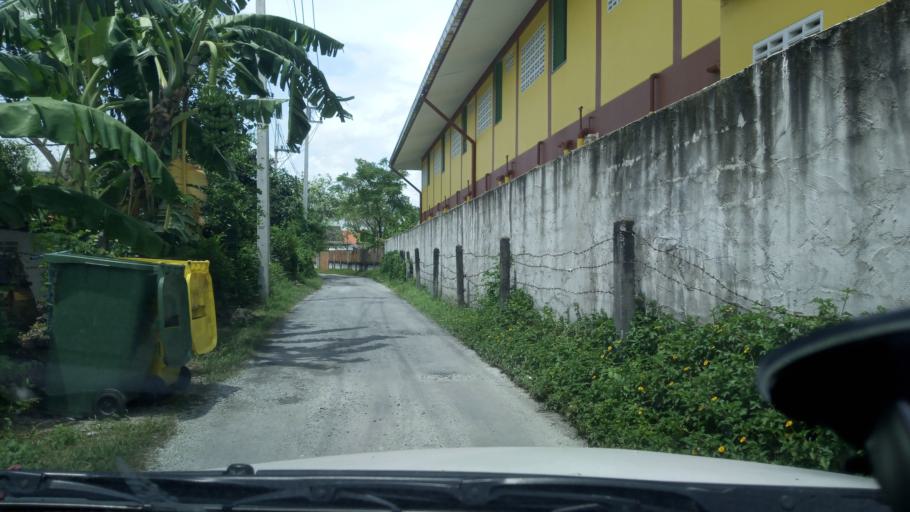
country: TH
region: Chon Buri
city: Phan Thong
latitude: 13.4136
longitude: 101.0516
